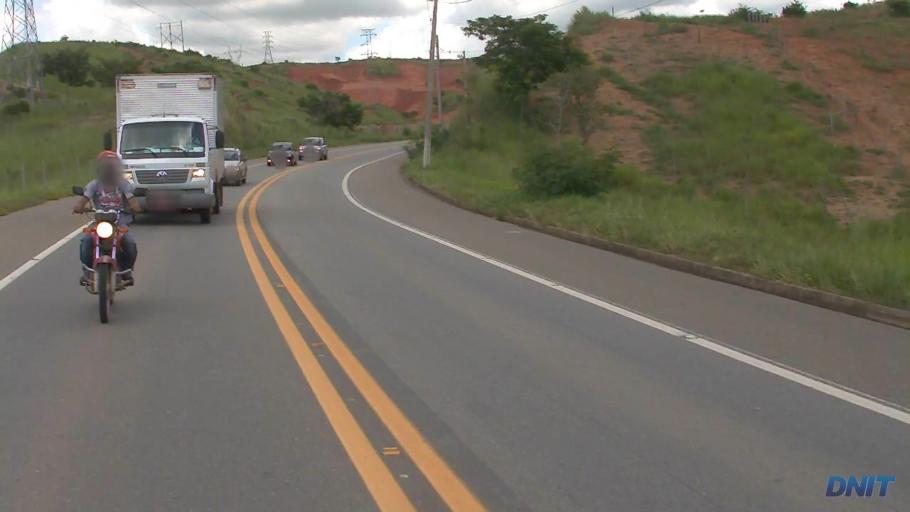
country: BR
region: Minas Gerais
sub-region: Governador Valadares
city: Governador Valadares
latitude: -18.8722
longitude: -41.9919
